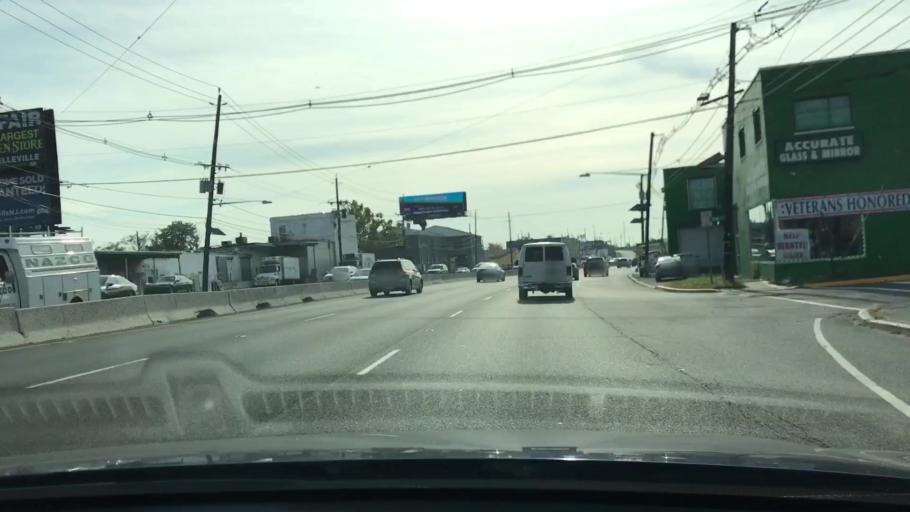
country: US
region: New Jersey
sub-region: Bergen County
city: Carlstadt
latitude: 40.8373
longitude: -74.0846
